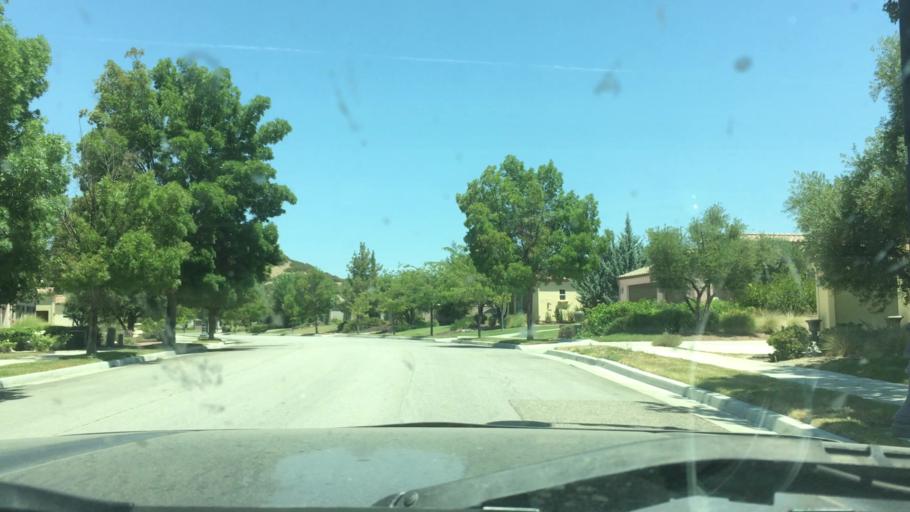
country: US
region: California
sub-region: San Luis Obispo County
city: Paso Robles
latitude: 35.6260
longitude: -120.6604
